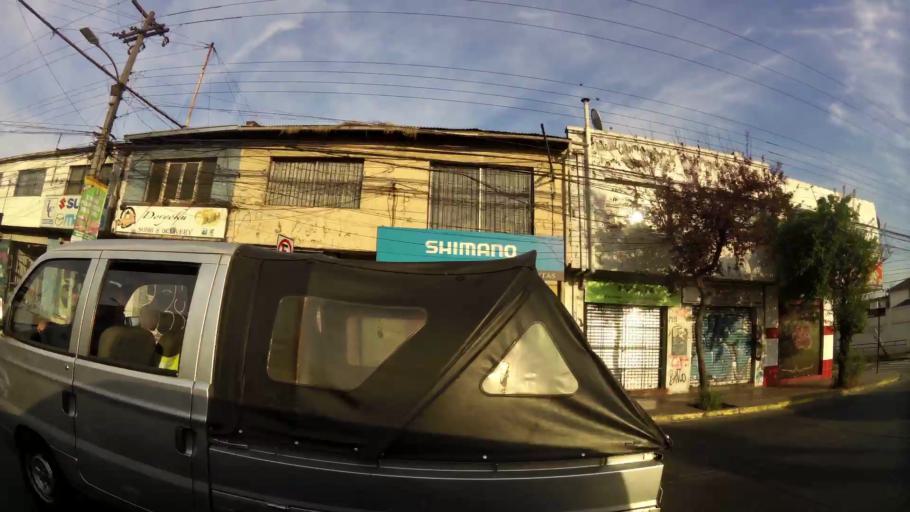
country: CL
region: Santiago Metropolitan
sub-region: Provincia de Santiago
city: Santiago
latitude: -33.5216
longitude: -70.6602
